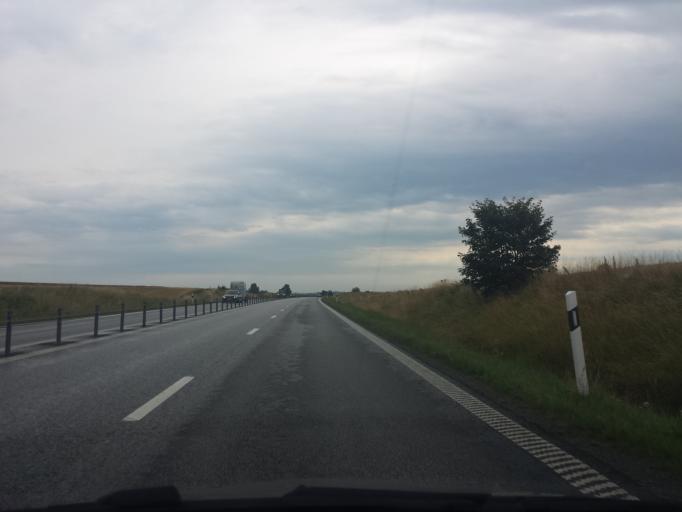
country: SE
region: Skane
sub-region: Skurups Kommun
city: Skurup
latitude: 55.4921
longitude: 13.5284
